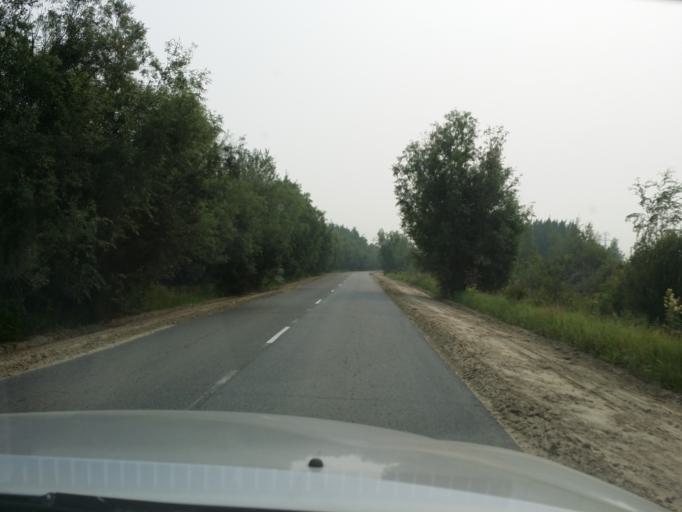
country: RU
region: Khanty-Mansiyskiy Avtonomnyy Okrug
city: Megion
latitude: 60.9948
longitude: 76.3011
